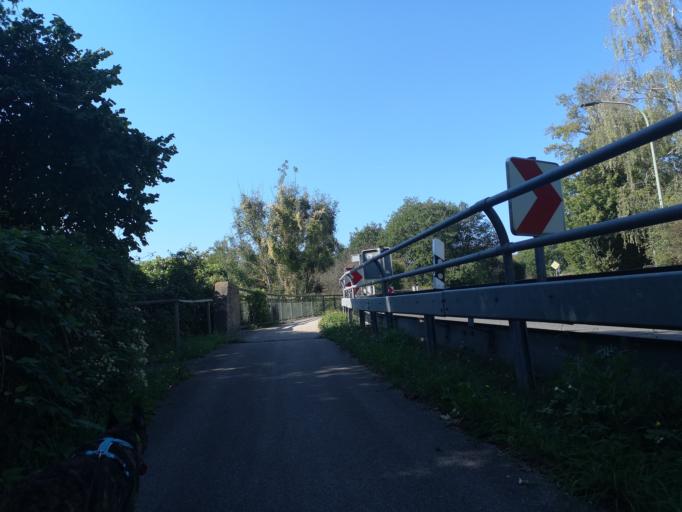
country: DE
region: North Rhine-Westphalia
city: Heimbach
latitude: 50.6607
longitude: 6.4851
